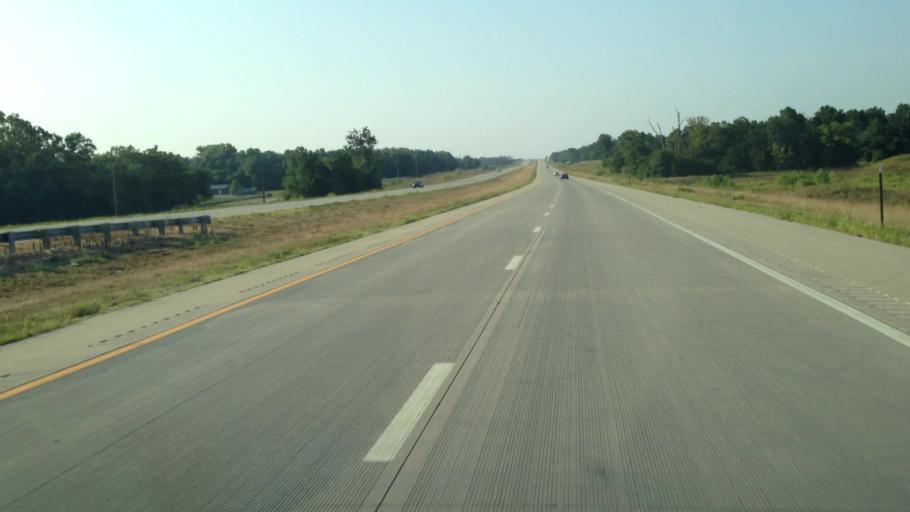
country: US
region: Kansas
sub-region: Douglas County
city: Baldwin City
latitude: 38.7414
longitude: -95.2673
